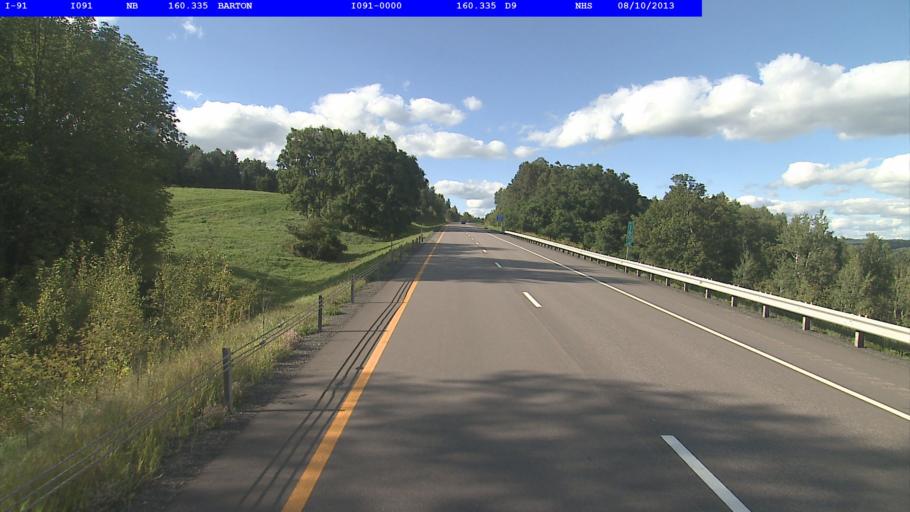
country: US
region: Vermont
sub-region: Orleans County
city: Newport
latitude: 44.7912
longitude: -72.2155
